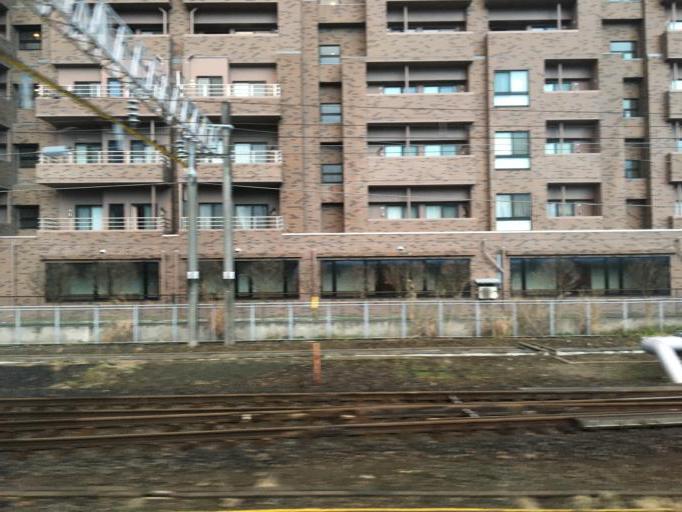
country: JP
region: Aomori
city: Aomori Shi
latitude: 40.8276
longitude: 140.7332
